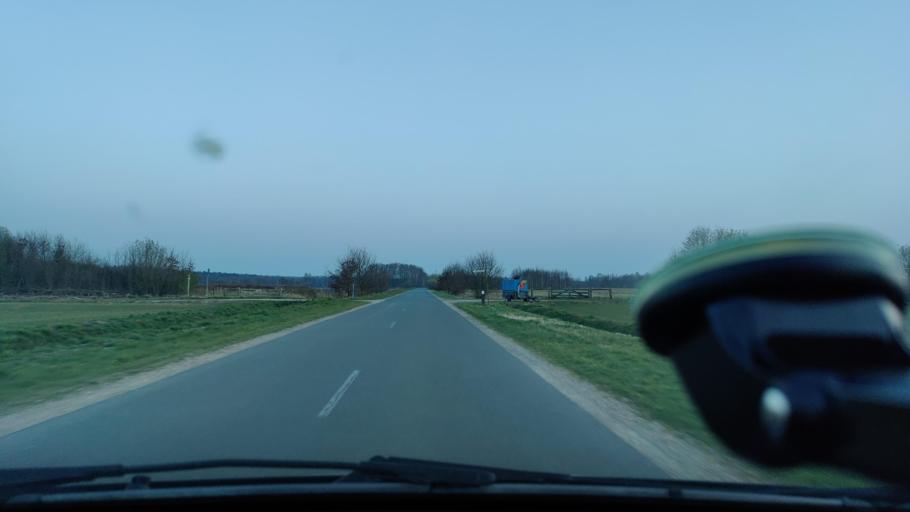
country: NL
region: Limburg
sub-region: Gemeente Bergen
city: Wellerlooi
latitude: 51.5355
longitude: 6.1750
